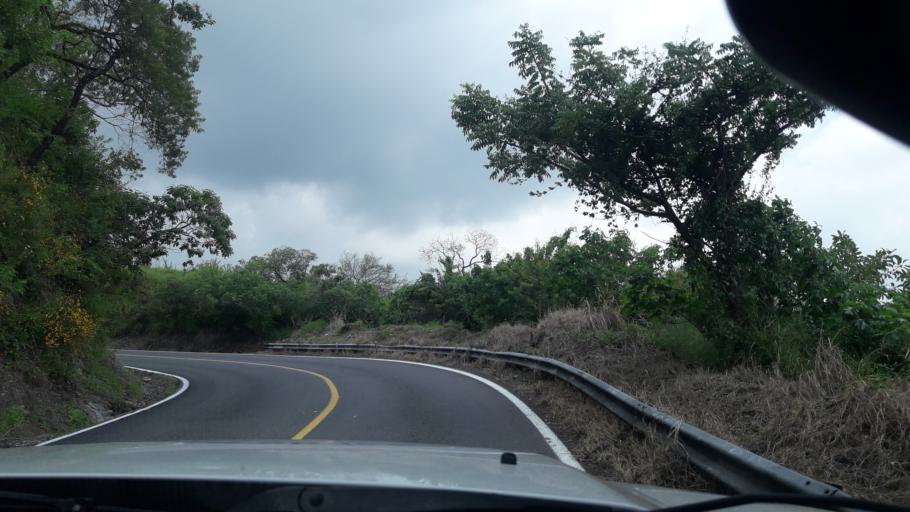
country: MX
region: Colima
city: Suchitlan
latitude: 19.4342
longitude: -103.7119
